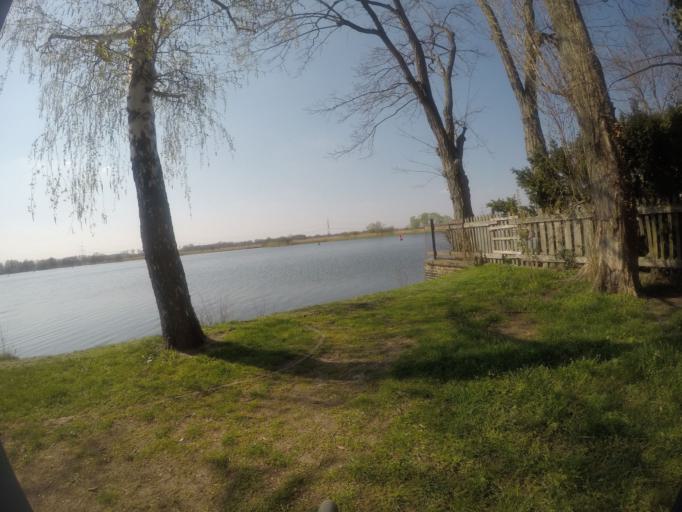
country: DE
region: Brandenburg
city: Ketzin
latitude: 52.4757
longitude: 12.8392
